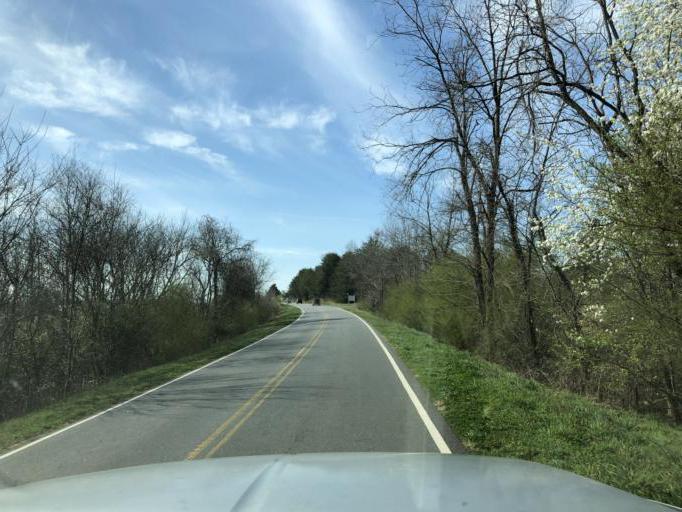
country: US
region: North Carolina
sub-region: Burke County
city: Salem
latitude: 35.5001
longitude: -81.6321
